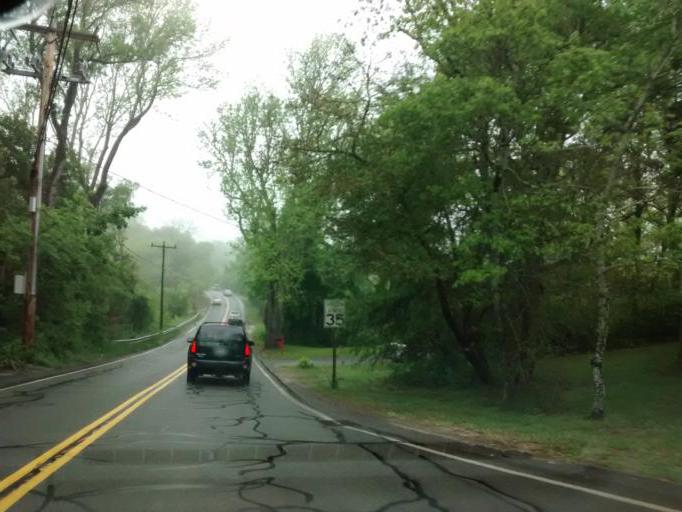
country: US
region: Massachusetts
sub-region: Barnstable County
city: Pocasset
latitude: 41.6959
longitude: -70.6050
